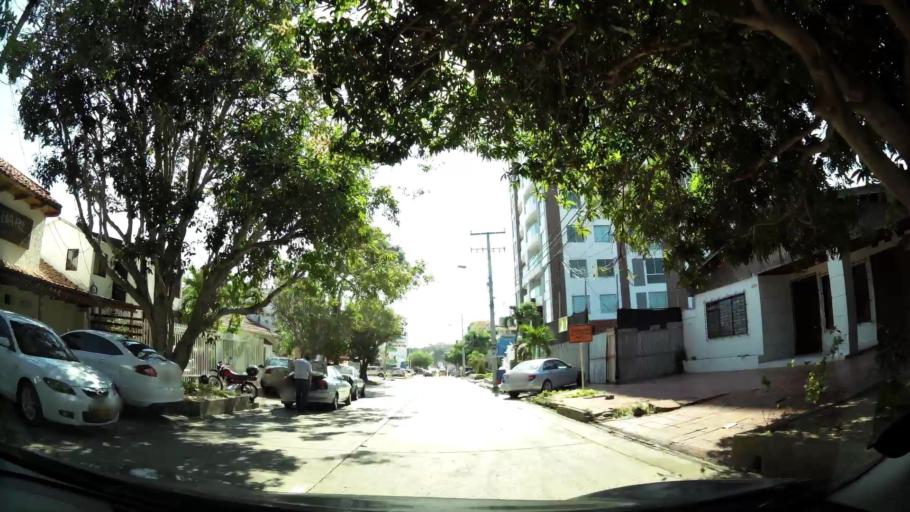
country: CO
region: Atlantico
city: Barranquilla
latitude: 10.9988
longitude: -74.8102
